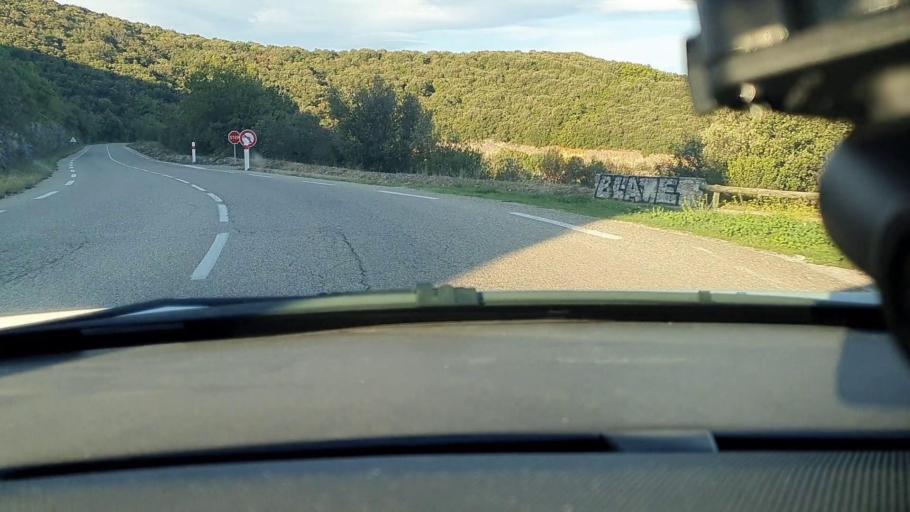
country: FR
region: Languedoc-Roussillon
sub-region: Departement du Gard
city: Barjac
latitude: 44.2295
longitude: 4.3177
